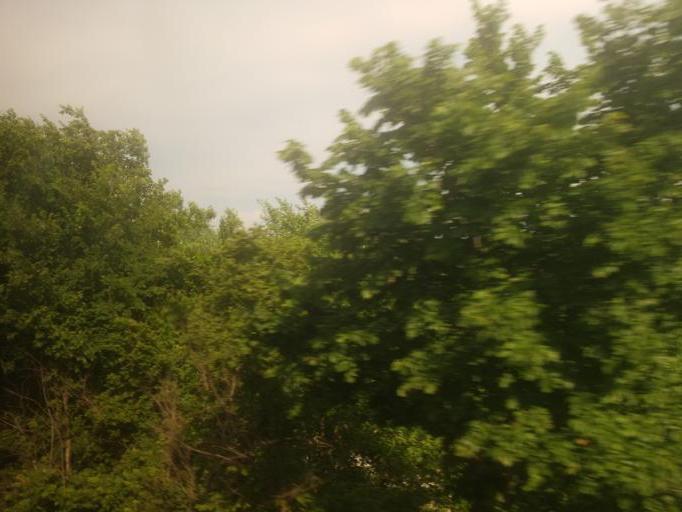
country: US
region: Illinois
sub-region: Henry County
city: Galva
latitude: 41.1068
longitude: -90.1724
